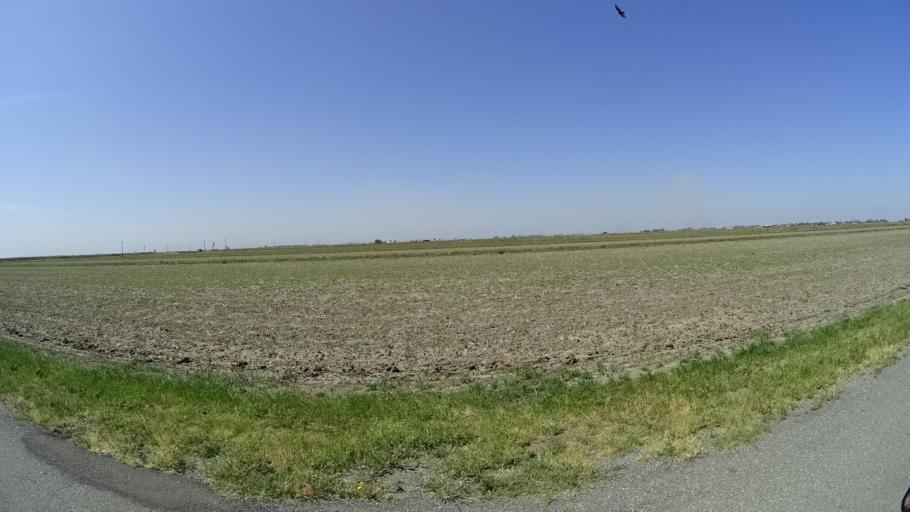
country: US
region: California
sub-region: Glenn County
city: Willows
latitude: 39.5595
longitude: -122.0179
